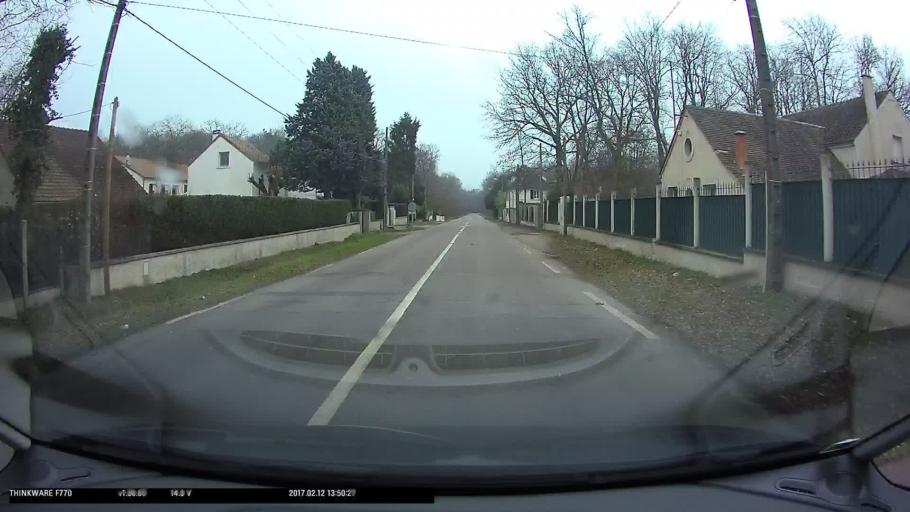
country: FR
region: Ile-de-France
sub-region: Departement des Yvelines
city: Triel-sur-Seine
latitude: 48.9936
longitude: 2.0207
